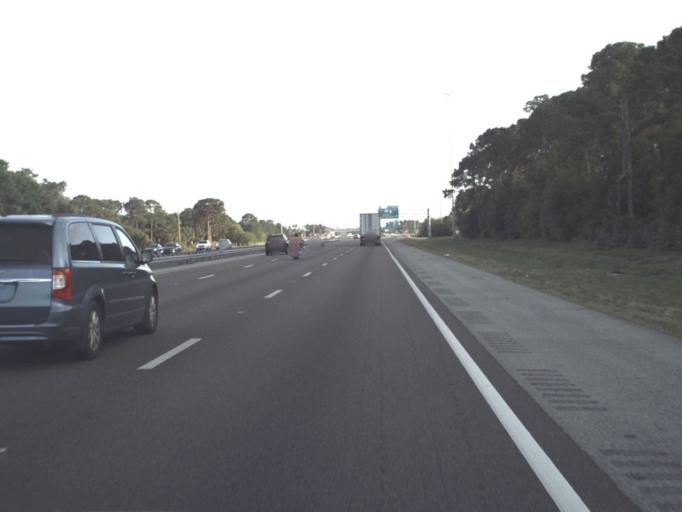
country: US
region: Florida
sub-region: Brevard County
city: Sharpes
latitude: 28.4221
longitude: -80.8205
